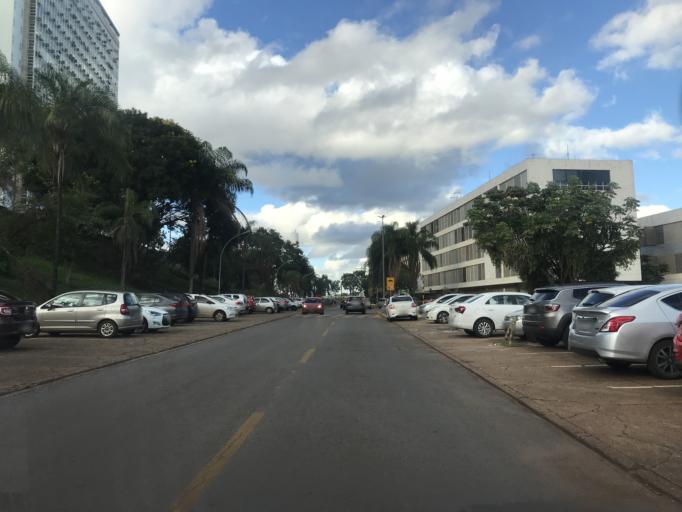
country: BR
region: Federal District
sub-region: Brasilia
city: Brasilia
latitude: -15.7998
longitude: -47.8806
